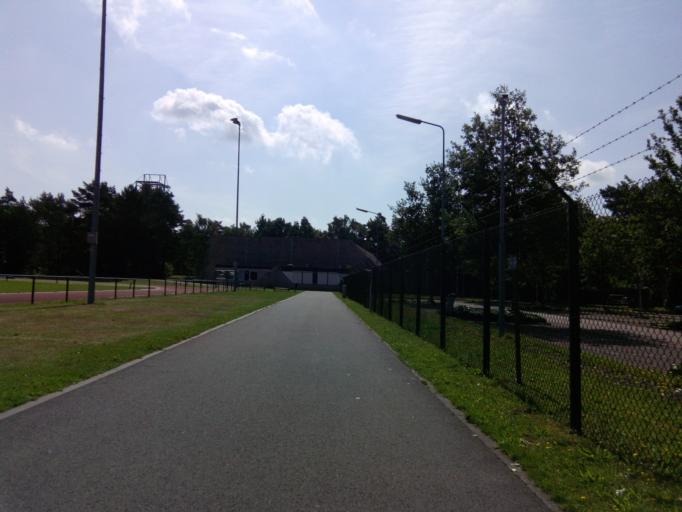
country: NL
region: Utrecht
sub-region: Gemeente Utrechtse Heuvelrug
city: Doorn
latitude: 52.0442
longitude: 5.3280
